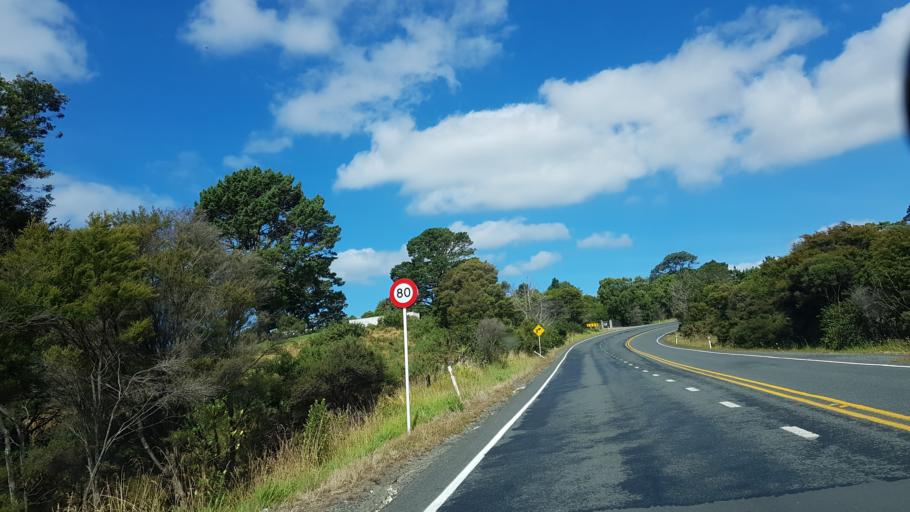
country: NZ
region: Auckland
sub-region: Auckland
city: Rothesay Bay
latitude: -36.6850
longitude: 174.7031
